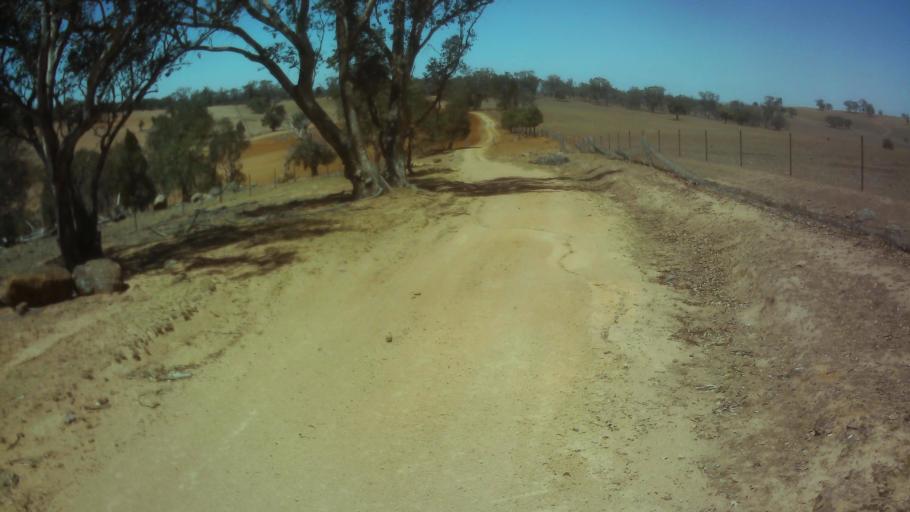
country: AU
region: New South Wales
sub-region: Cowra
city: Cowra
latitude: -33.9052
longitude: 148.5090
